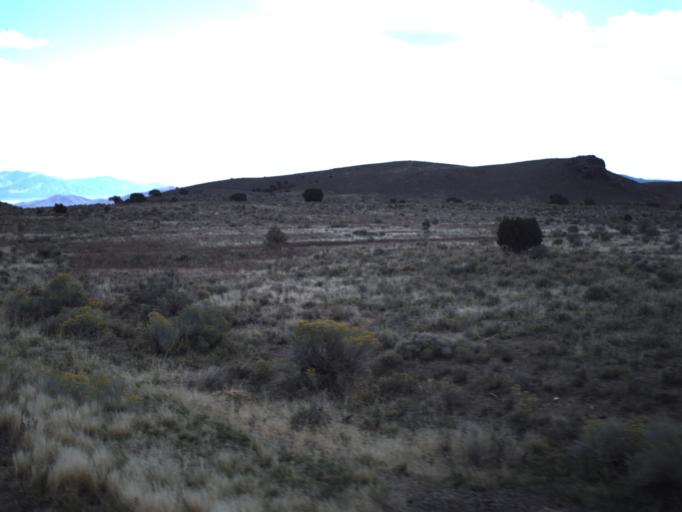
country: US
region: Utah
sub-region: Beaver County
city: Milford
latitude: 38.4611
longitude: -113.2361
